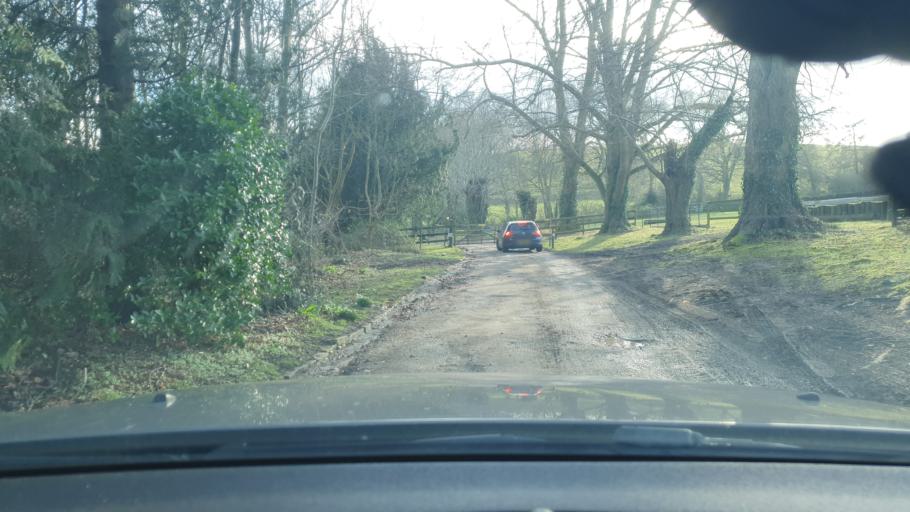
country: GB
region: England
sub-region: Royal Borough of Windsor and Maidenhead
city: Hurley
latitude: 51.5343
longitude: -0.8422
